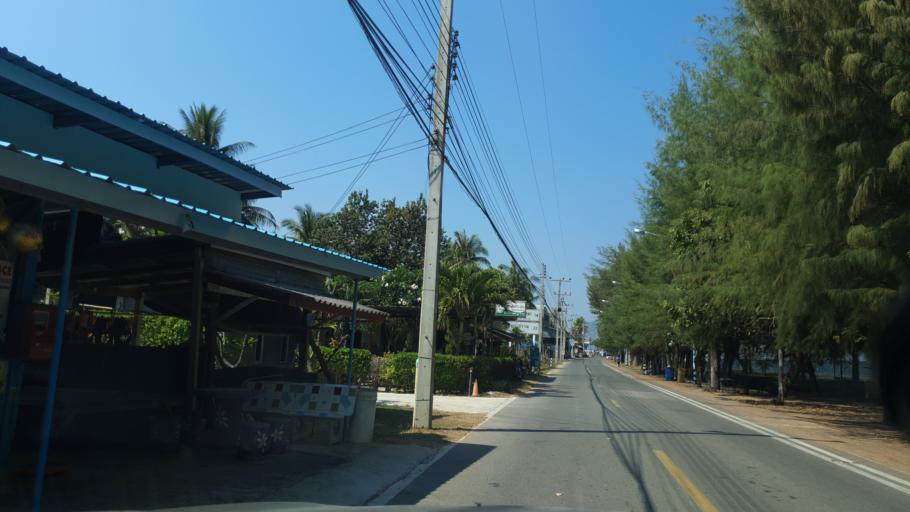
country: TH
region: Prachuap Khiri Khan
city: Sam Roi Yot
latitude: 12.2336
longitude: 99.9930
